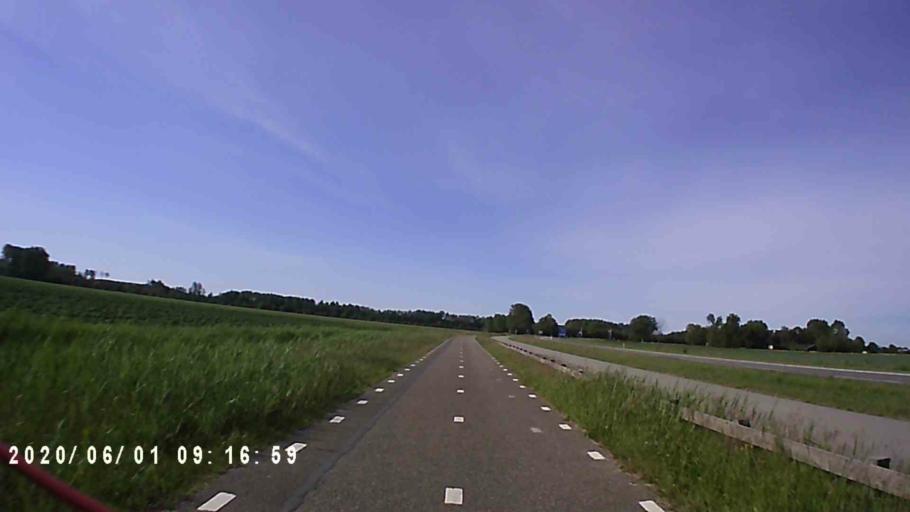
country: NL
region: Friesland
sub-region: Gemeente Leeuwarderadeel
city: Stiens
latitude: 53.2747
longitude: 5.7616
